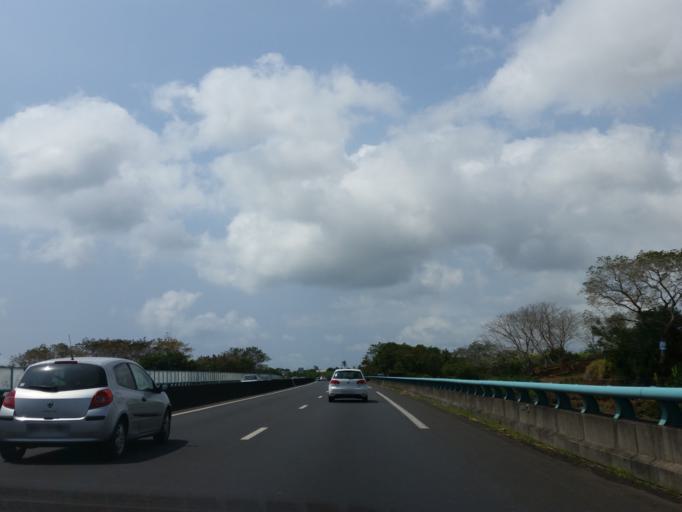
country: RE
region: Reunion
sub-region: Reunion
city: Sainte-Marie
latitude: -20.9028
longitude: 55.5519
